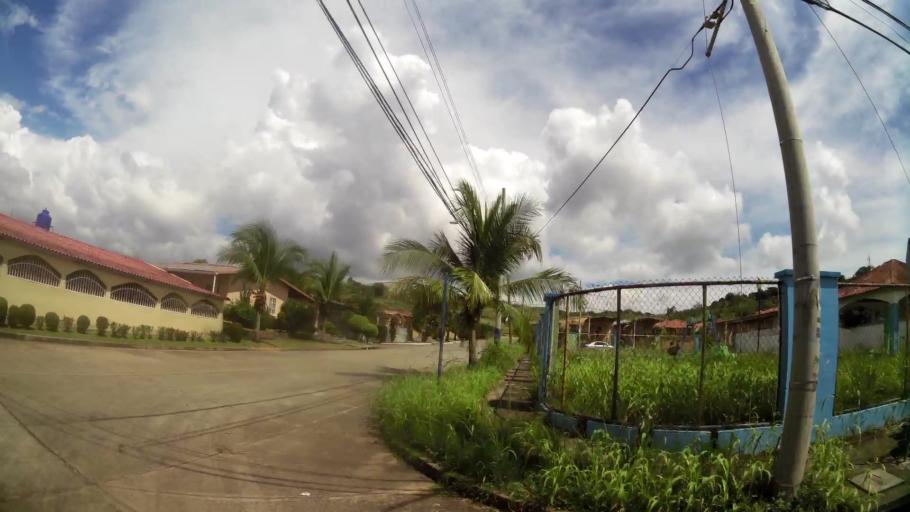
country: PA
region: Panama
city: San Vicente de Bique
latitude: 8.9198
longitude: -79.6903
